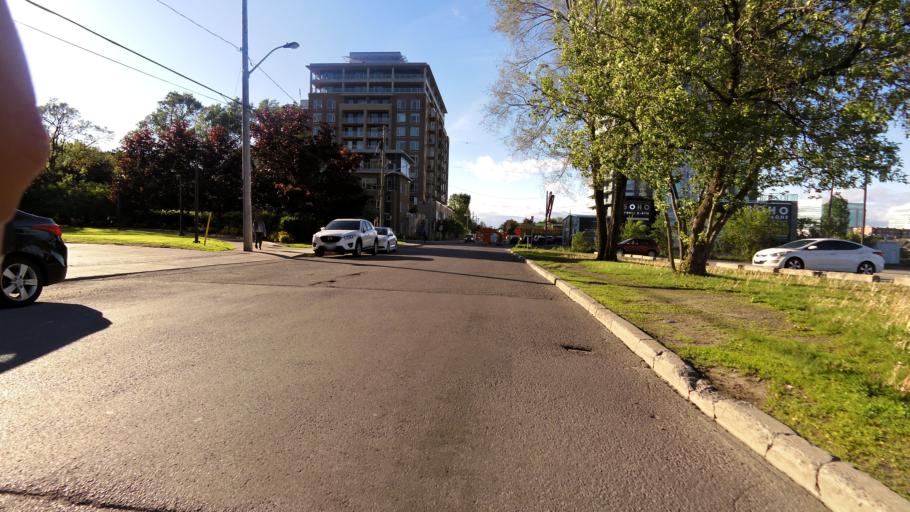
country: CA
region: Ontario
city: Ottawa
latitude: 45.3974
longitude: -75.7109
